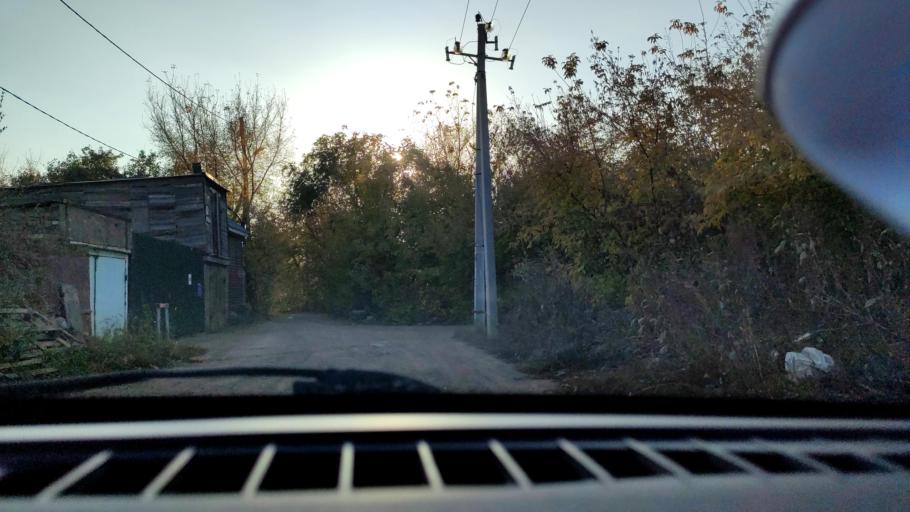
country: RU
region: Samara
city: Samara
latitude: 53.1815
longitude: 50.2230
